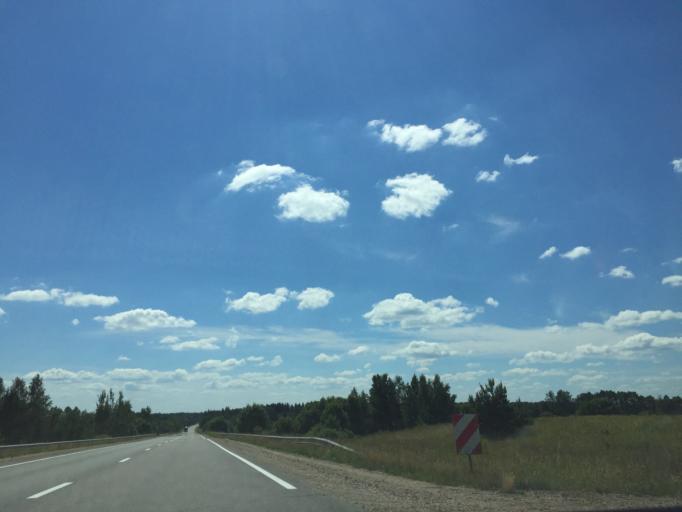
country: LV
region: Rezekne
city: Rezekne
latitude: 56.5261
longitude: 27.2751
